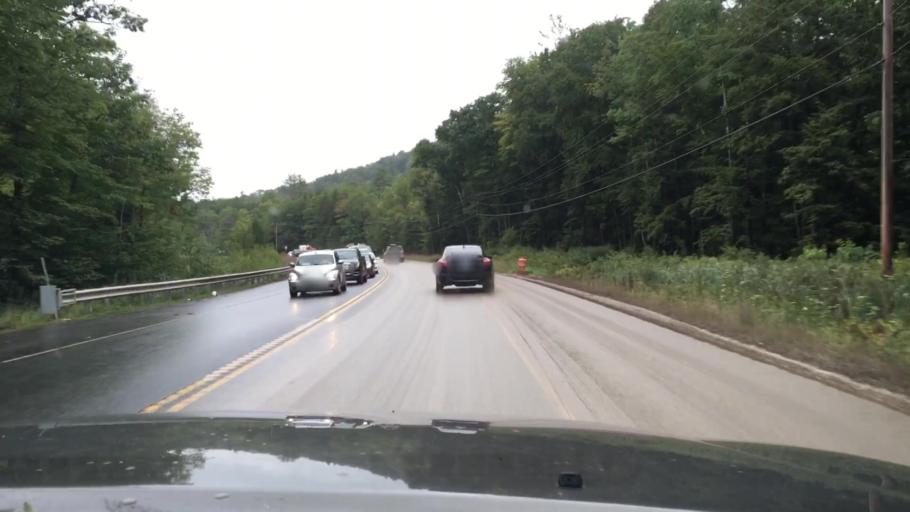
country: US
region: New Hampshire
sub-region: Cheshire County
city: Marlborough
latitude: 42.9717
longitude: -72.2145
